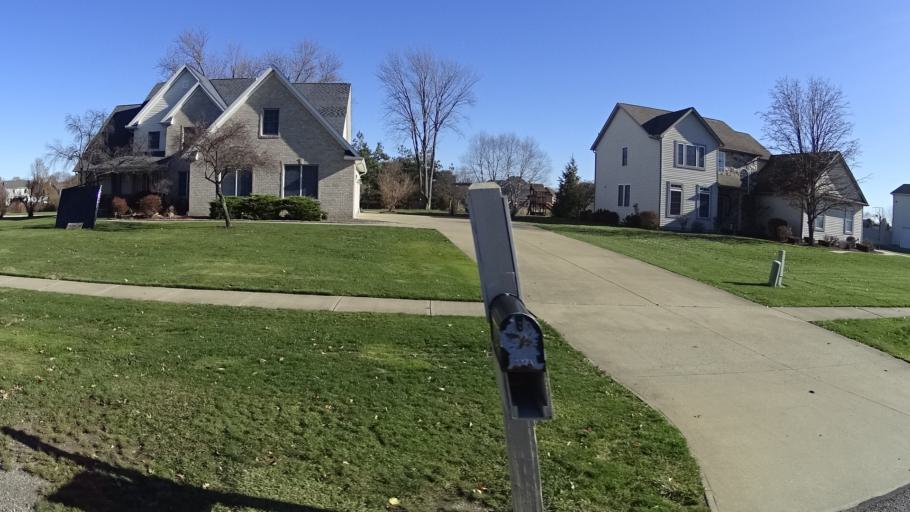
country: US
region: Ohio
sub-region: Lorain County
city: Avon Center
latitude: 41.4267
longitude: -82.0038
